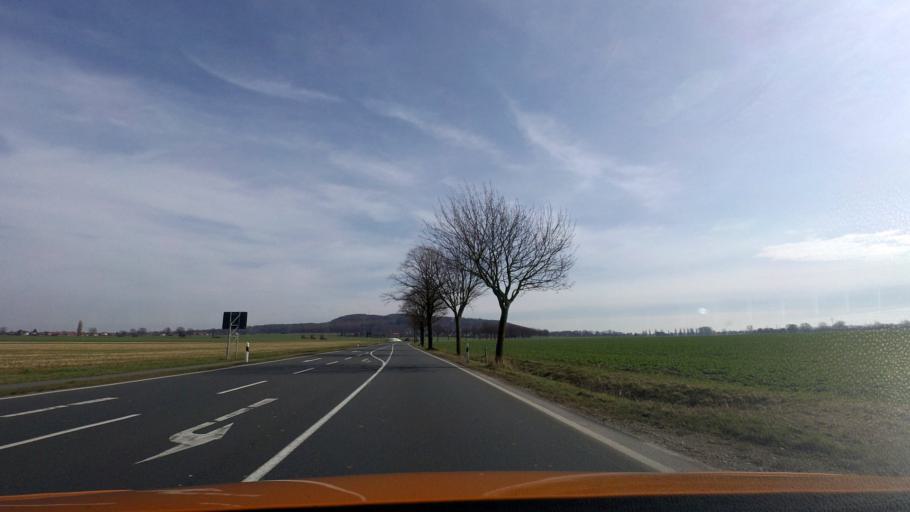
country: DE
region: Lower Saxony
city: Gehrden
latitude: 52.3342
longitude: 9.5867
